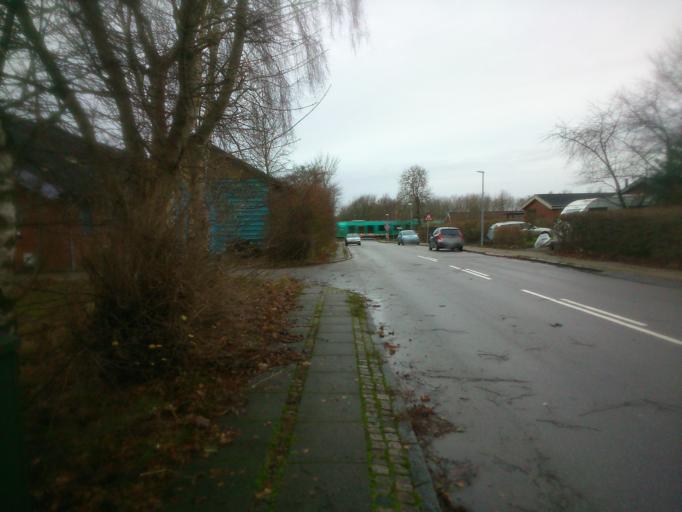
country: DK
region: Central Jutland
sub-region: Ikast-Brande Kommune
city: Ikast
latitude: 56.1435
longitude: 9.1653
